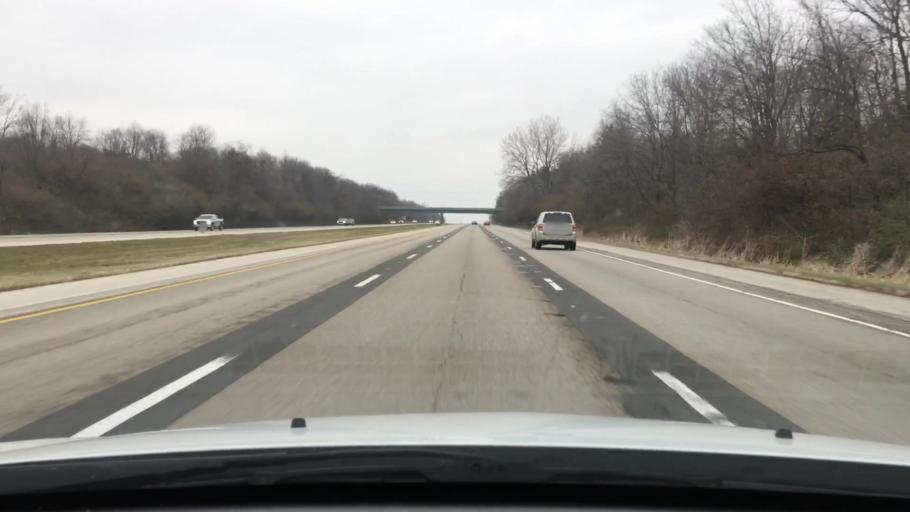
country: US
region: Illinois
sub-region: Logan County
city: Lincoln
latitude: 40.1433
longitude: -89.4170
